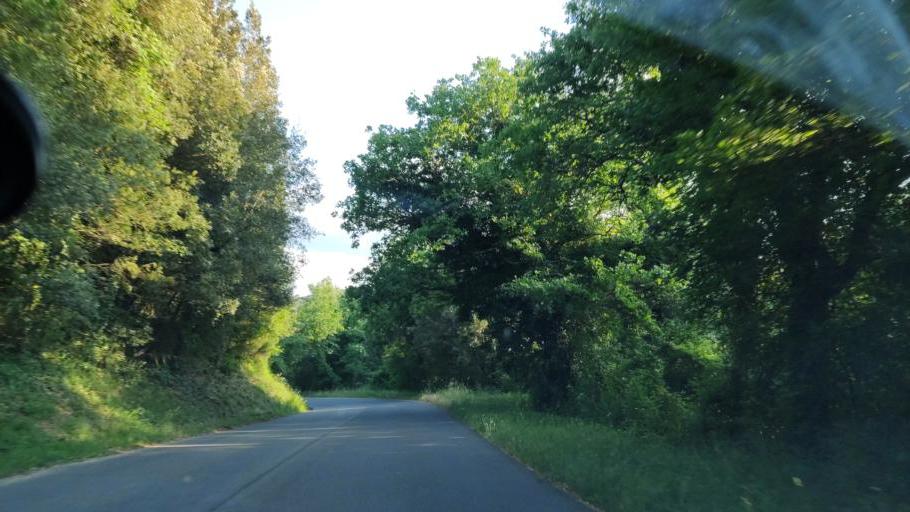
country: IT
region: Umbria
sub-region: Provincia di Terni
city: Lugnano in Teverina
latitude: 42.5888
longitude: 12.3775
